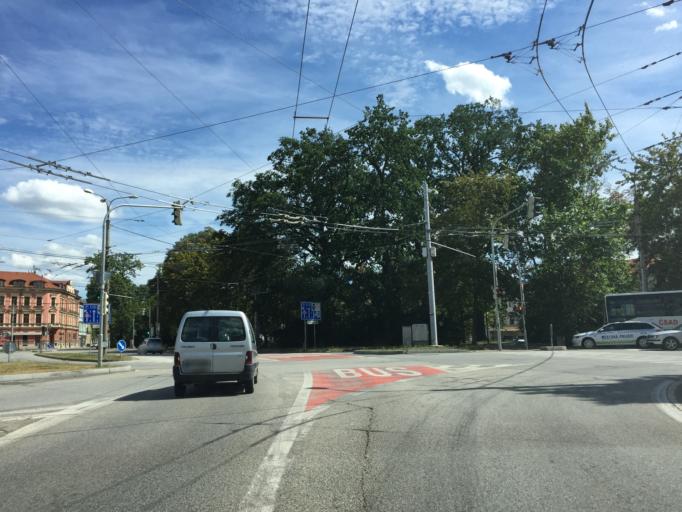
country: CZ
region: Jihocesky
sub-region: Okres Ceske Budejovice
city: Ceske Budejovice
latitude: 48.9787
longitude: 14.4728
